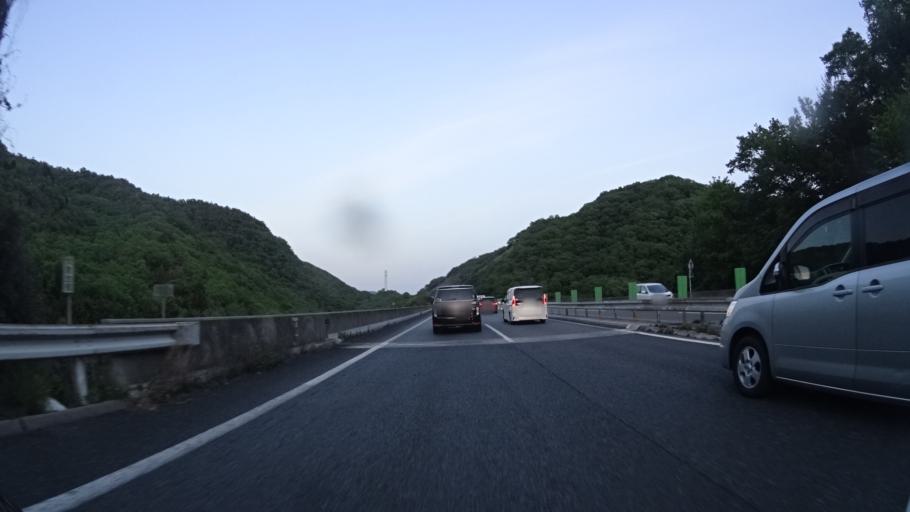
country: JP
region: Hyogo
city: Kariya
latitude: 34.7809
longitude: 134.2260
